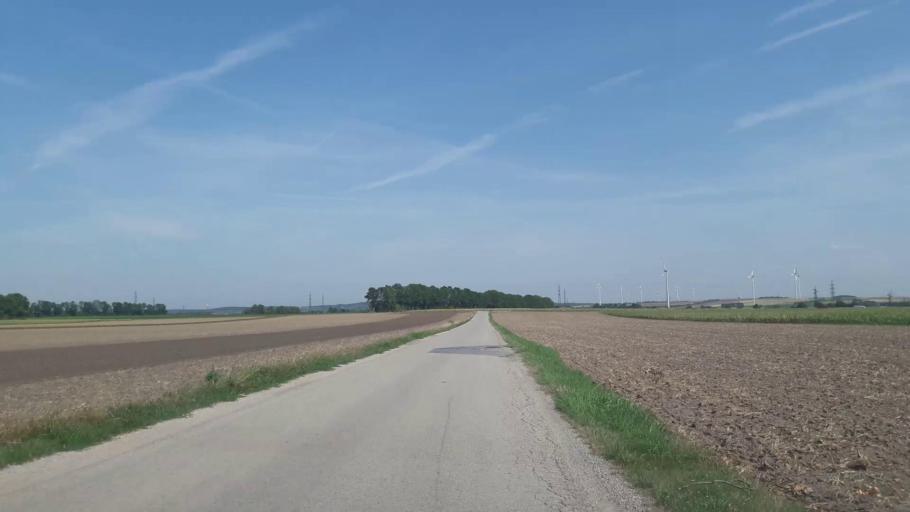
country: AT
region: Lower Austria
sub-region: Politischer Bezirk Bruck an der Leitha
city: Bruck an der Leitha
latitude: 48.0243
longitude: 16.7606
